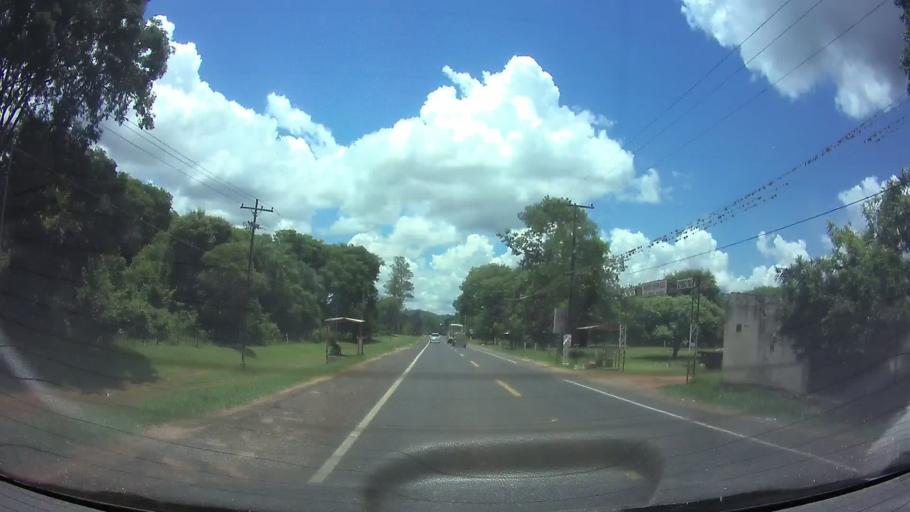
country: PY
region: Central
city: Capiata
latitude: -25.3557
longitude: -57.4226
